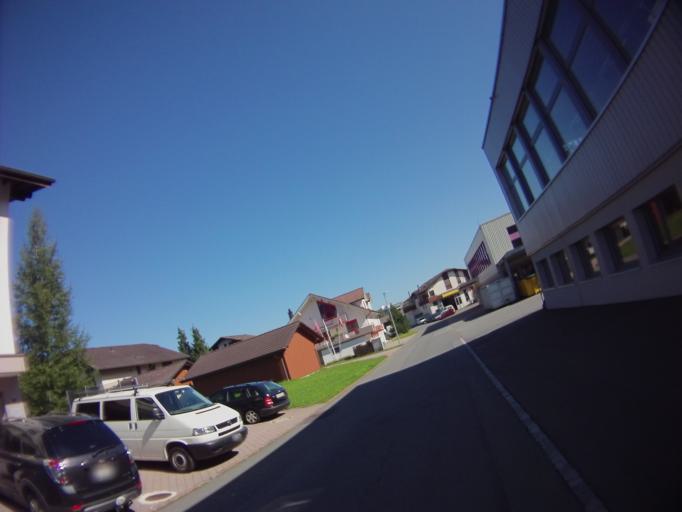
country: CH
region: Schwyz
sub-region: Bezirk Schwyz
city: Rothenthurm
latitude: 47.1019
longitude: 8.6730
